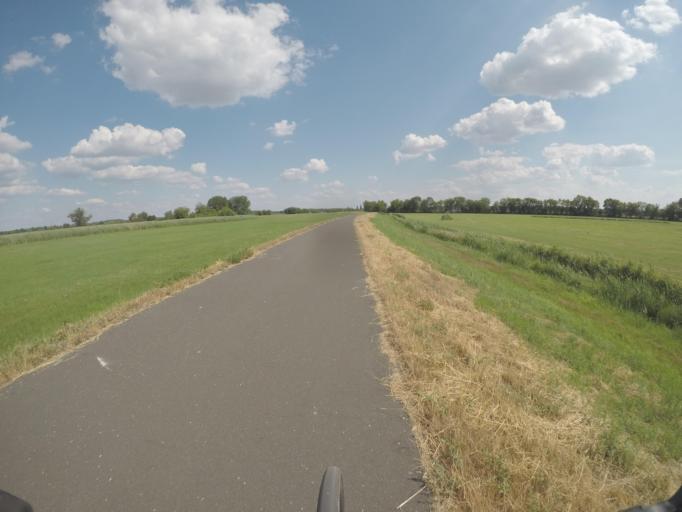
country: DE
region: Brandenburg
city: Ketzin
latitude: 52.4569
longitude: 12.8674
